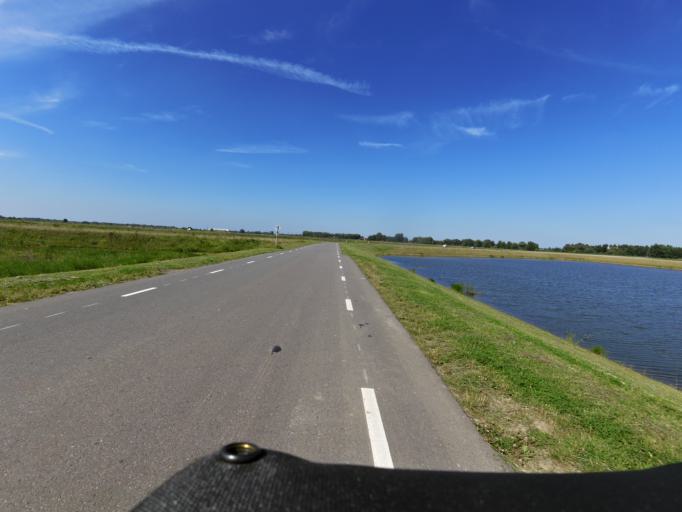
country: NL
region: North Brabant
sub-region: Gemeente Werkendam
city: Werkendam
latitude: 51.7860
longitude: 4.8675
